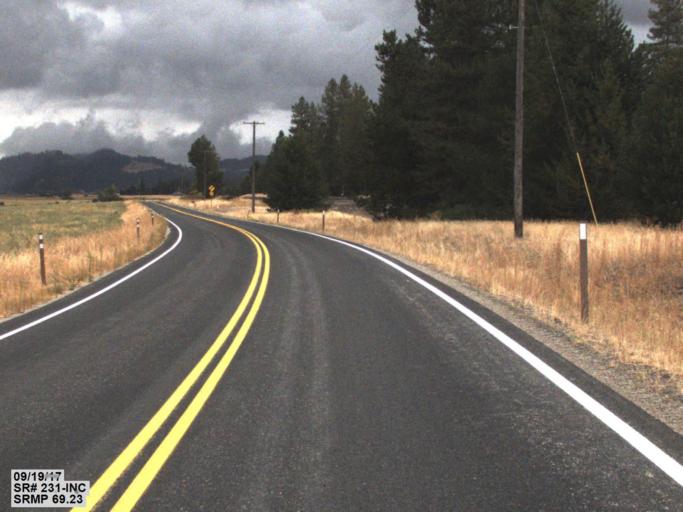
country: US
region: Washington
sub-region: Stevens County
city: Chewelah
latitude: 48.1399
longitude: -117.7315
